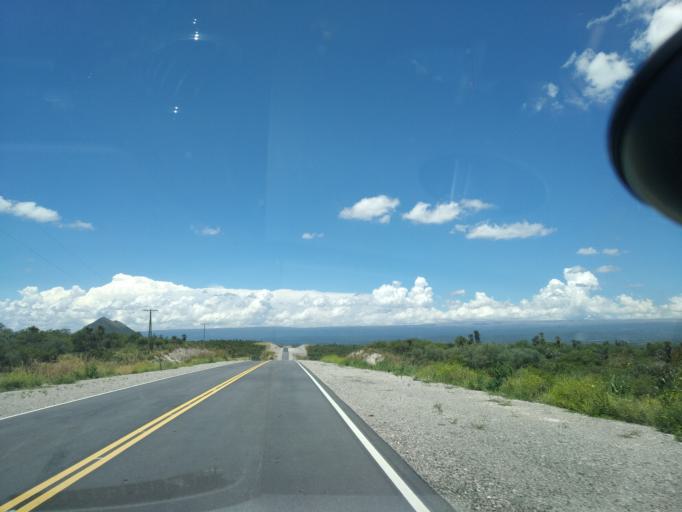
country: AR
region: Cordoba
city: Salsacate
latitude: -31.3636
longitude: -65.2039
